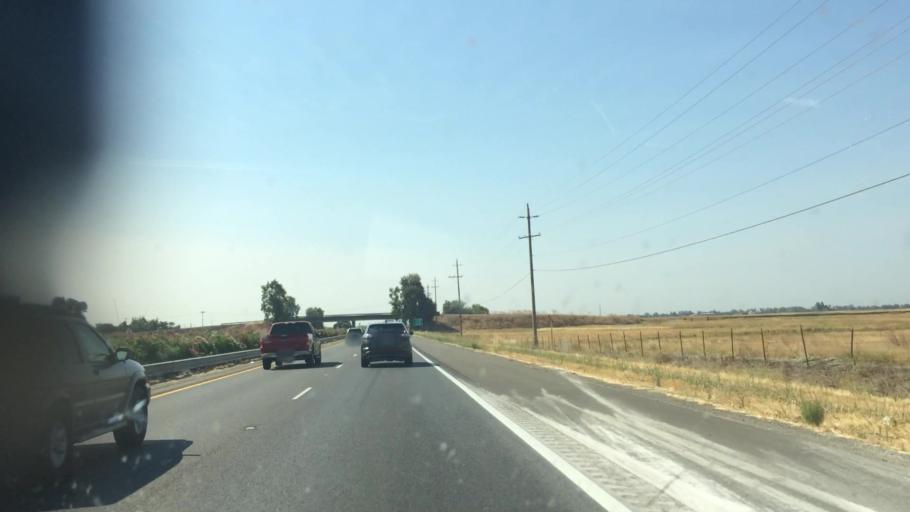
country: US
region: California
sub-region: Sacramento County
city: Galt
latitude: 38.3275
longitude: -121.3285
